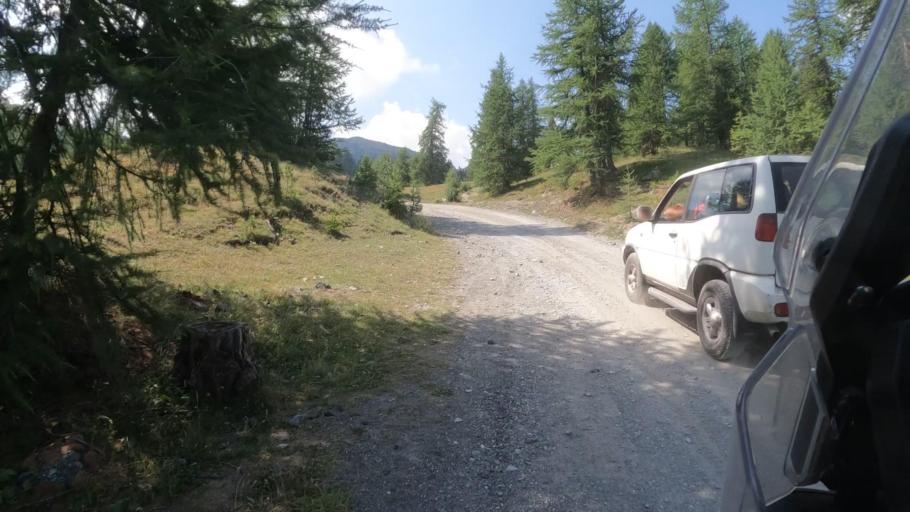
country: IT
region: Piedmont
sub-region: Provincia di Torino
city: Cesana Torinese
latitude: 44.9068
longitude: 6.7990
